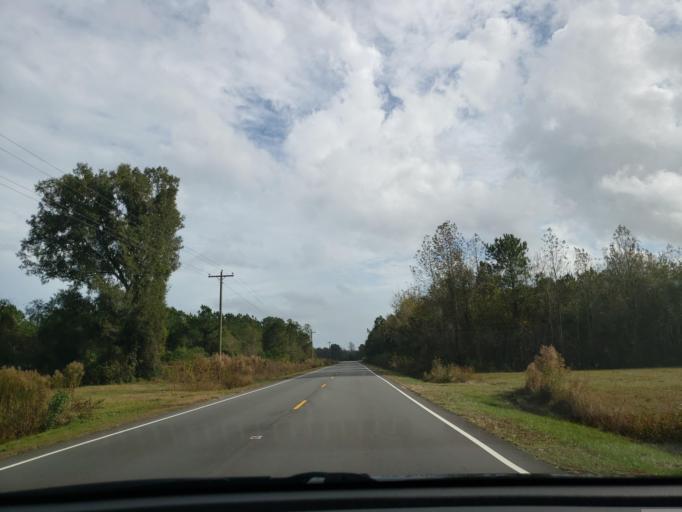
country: US
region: North Carolina
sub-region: Duplin County
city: Beulaville
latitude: 34.8281
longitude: -77.8461
